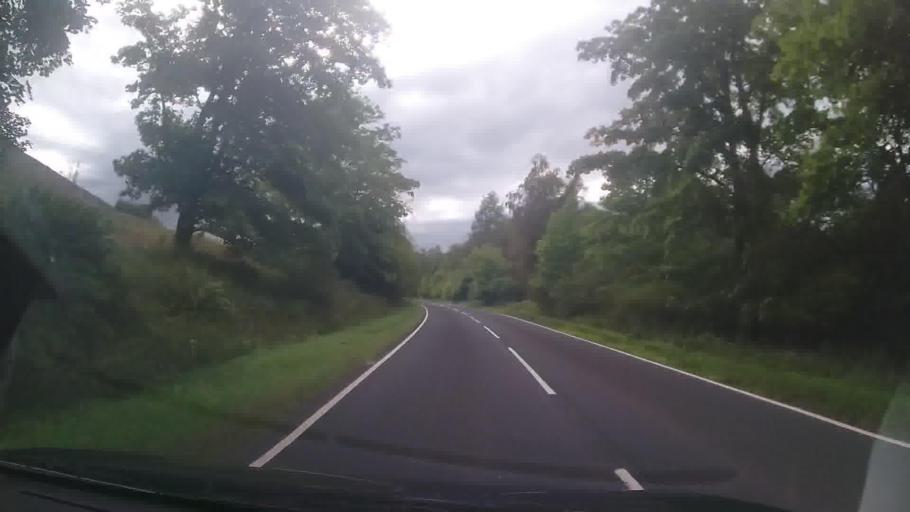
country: GB
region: Scotland
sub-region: Argyll and Bute
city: Garelochhead
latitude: 56.2463
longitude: -4.9410
